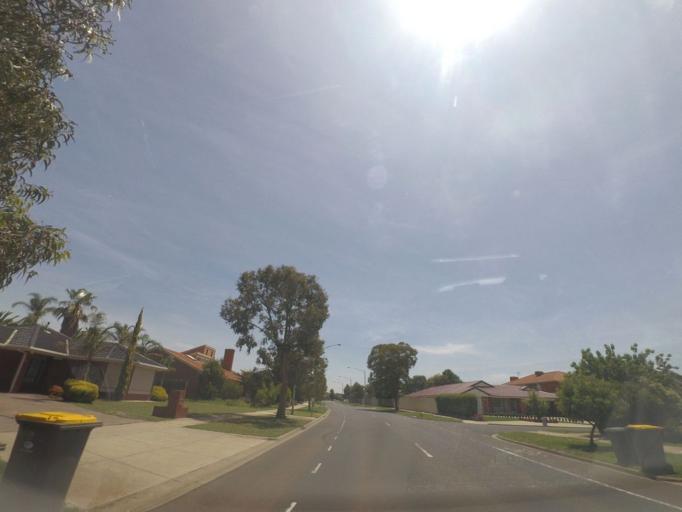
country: AU
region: Victoria
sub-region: Brimbank
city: Taylors Lakes
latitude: -37.7021
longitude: 144.7820
